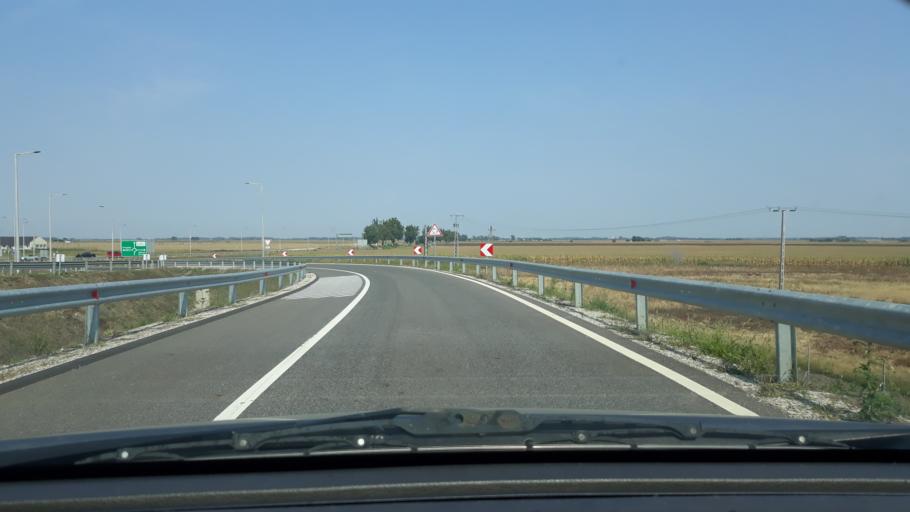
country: HU
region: Hajdu-Bihar
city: Berettyoujfalu
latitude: 47.2739
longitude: 21.5514
